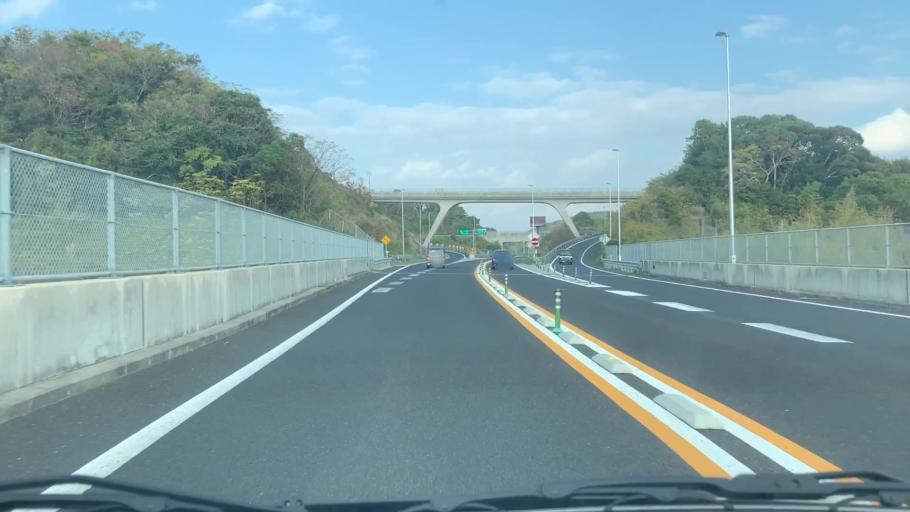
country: JP
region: Nagasaki
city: Sasebo
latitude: 33.0418
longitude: 129.7465
